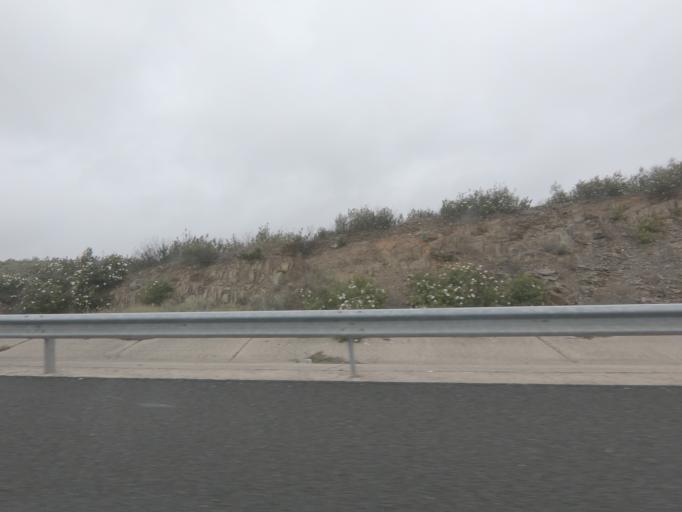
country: ES
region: Extremadura
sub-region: Provincia de Caceres
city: Canaveral
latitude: 39.7787
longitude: -6.3830
